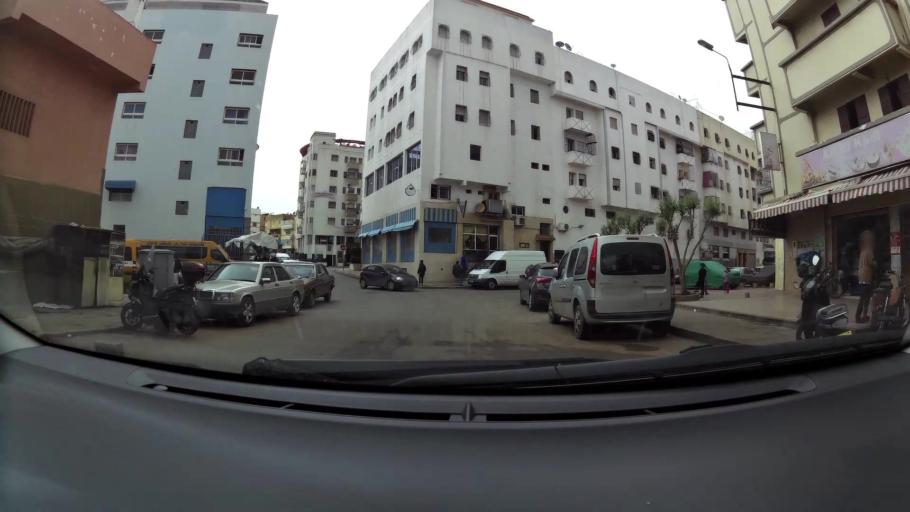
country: MA
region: Grand Casablanca
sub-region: Casablanca
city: Casablanca
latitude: 33.5611
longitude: -7.5600
